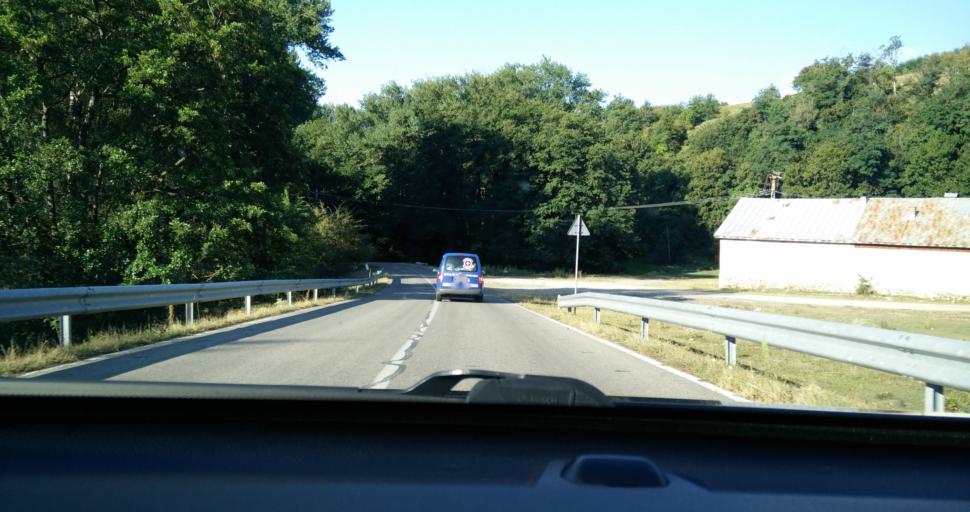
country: RO
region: Gorj
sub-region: Comuna Polovragi
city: Polovragi
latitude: 45.1790
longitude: 23.7852
